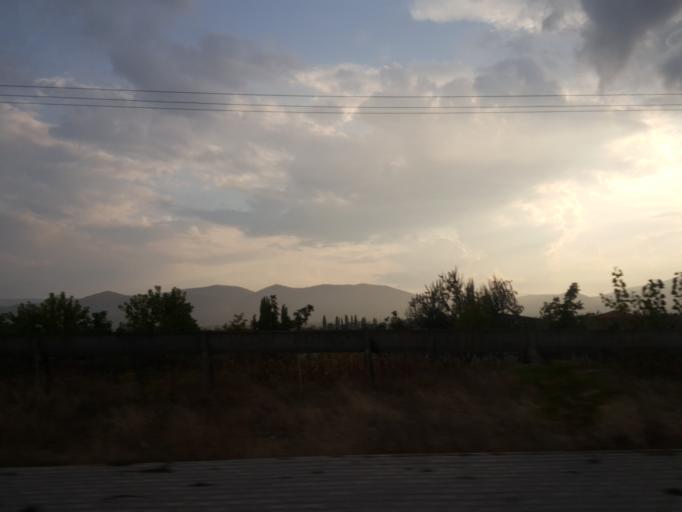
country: TR
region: Amasya
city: Gumushacikoy
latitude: 40.8764
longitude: 35.2334
